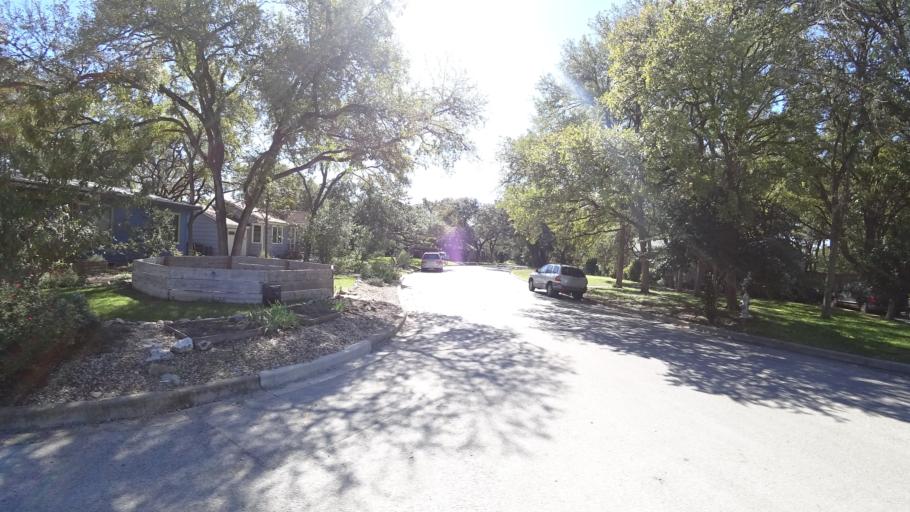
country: US
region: Texas
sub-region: Travis County
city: Austin
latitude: 30.3218
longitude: -97.7459
